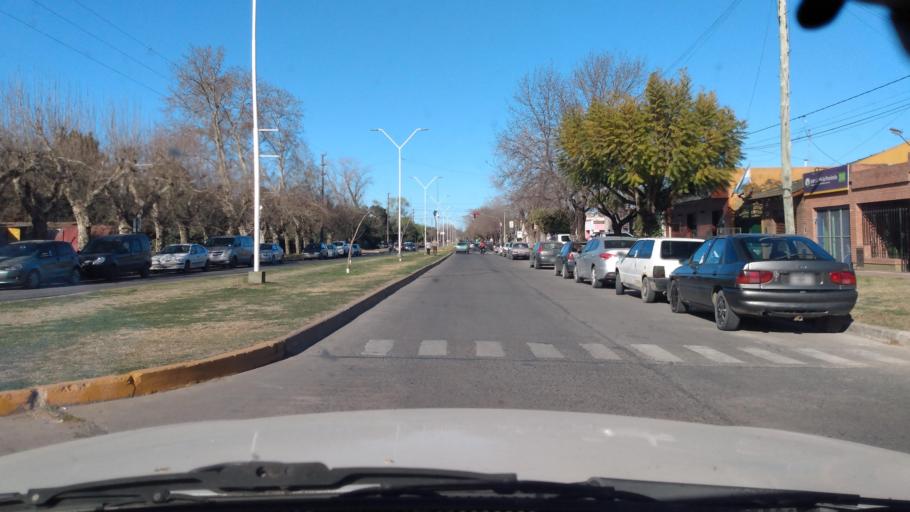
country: AR
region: Buenos Aires
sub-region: Partido de Mercedes
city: Mercedes
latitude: -34.6455
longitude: -59.4249
